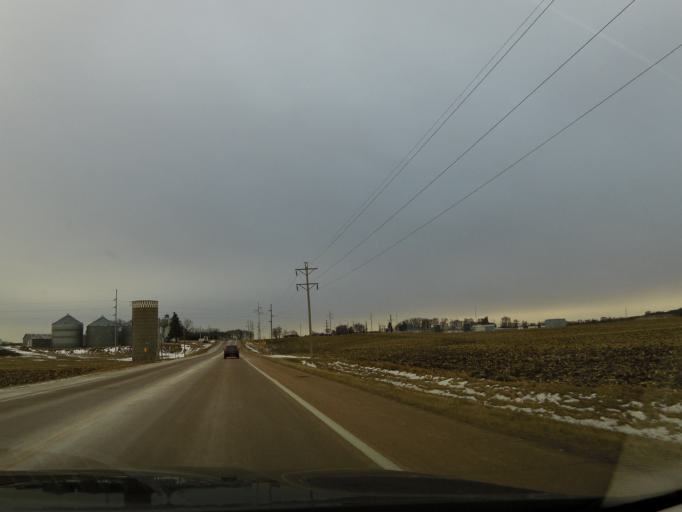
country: US
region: Minnesota
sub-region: Carver County
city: Watertown
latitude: 44.9099
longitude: -93.8217
